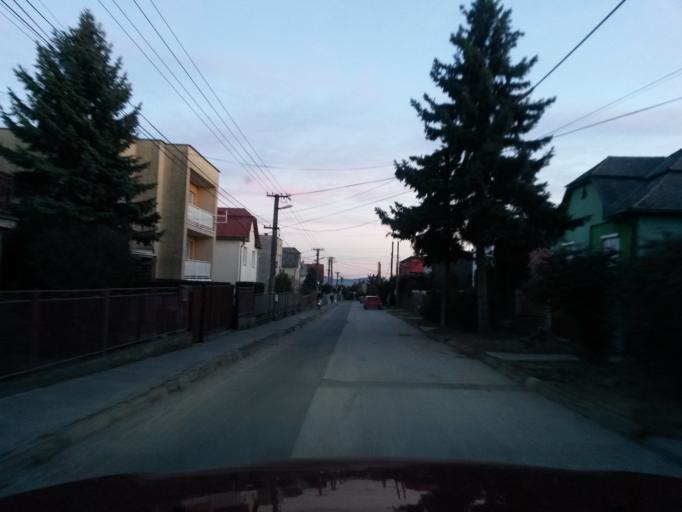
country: SK
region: Kosicky
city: Kosice
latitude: 48.7386
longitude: 21.2922
